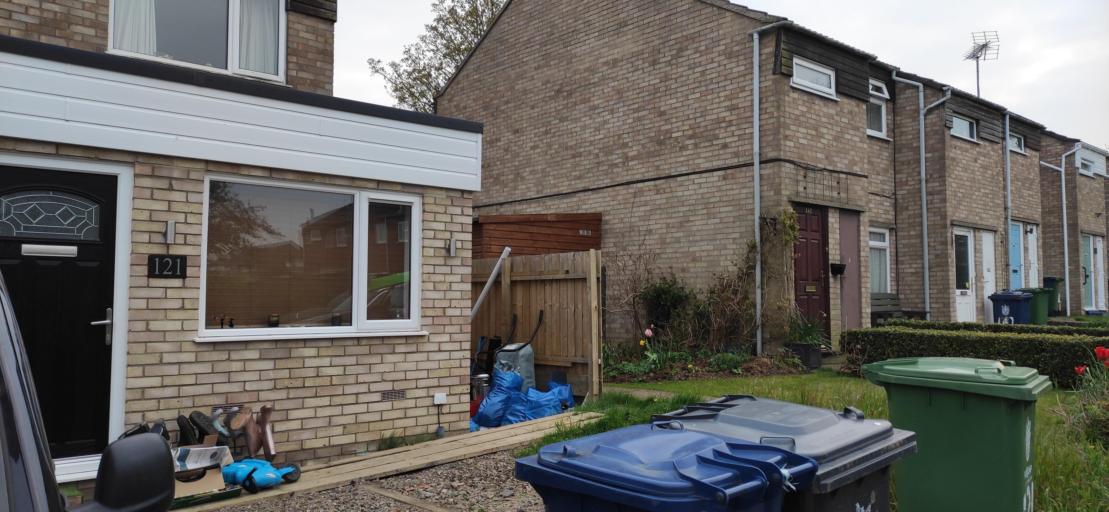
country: GB
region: England
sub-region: Cambridgeshire
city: Swavesey
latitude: 52.2500
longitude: 0.0131
